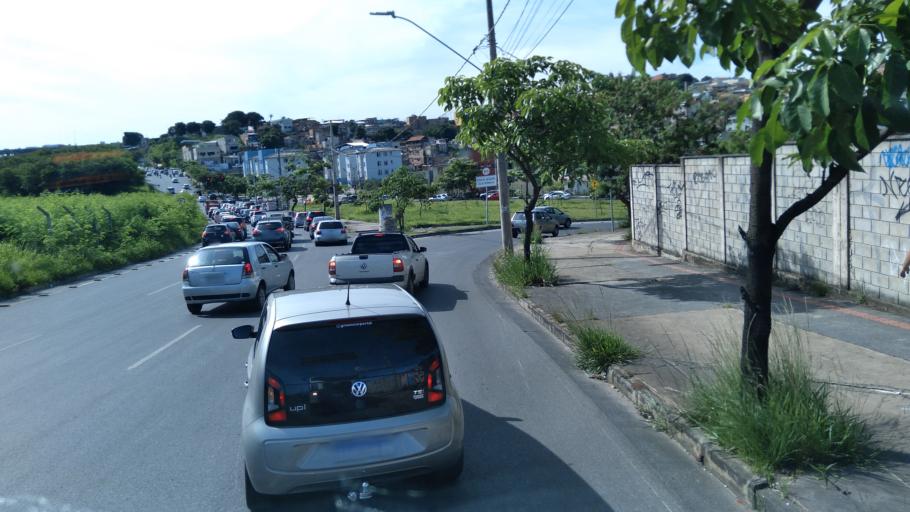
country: BR
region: Minas Gerais
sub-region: Belo Horizonte
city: Belo Horizonte
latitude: -19.9004
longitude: -43.9928
